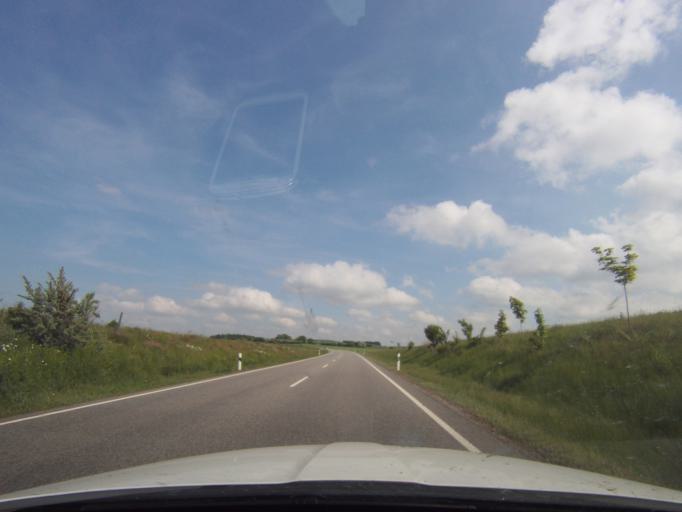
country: DE
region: Thuringia
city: Miesitz
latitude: 50.7381
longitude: 11.8232
